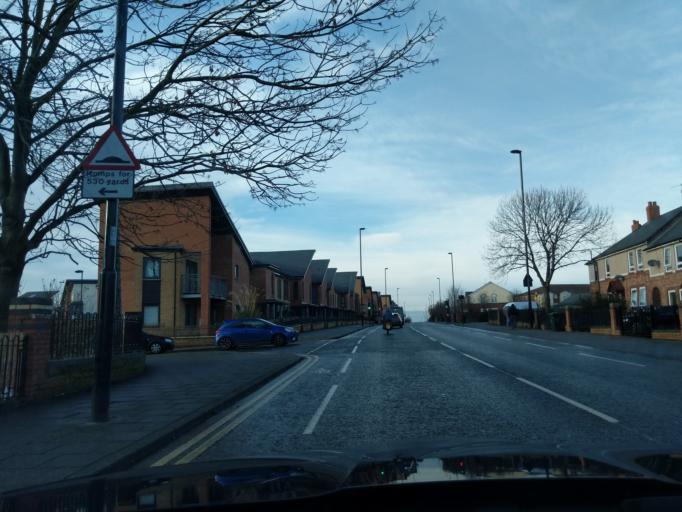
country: GB
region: England
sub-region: Gateshead
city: Felling
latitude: 54.9654
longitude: -1.5607
